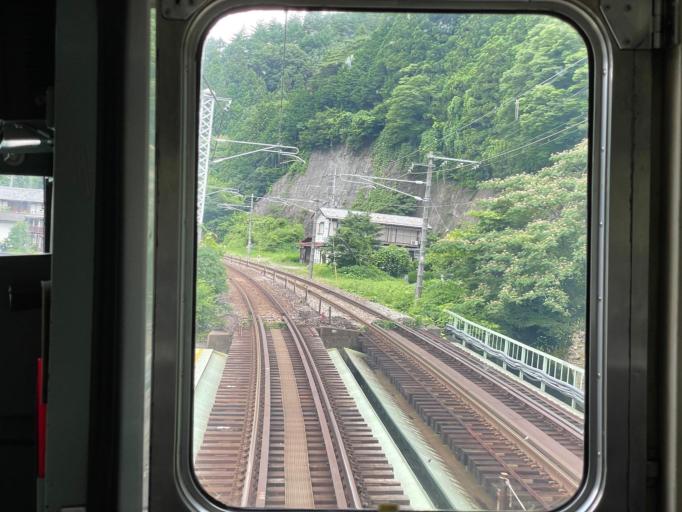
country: JP
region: Gunma
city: Numata
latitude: 36.7435
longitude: 138.9863
